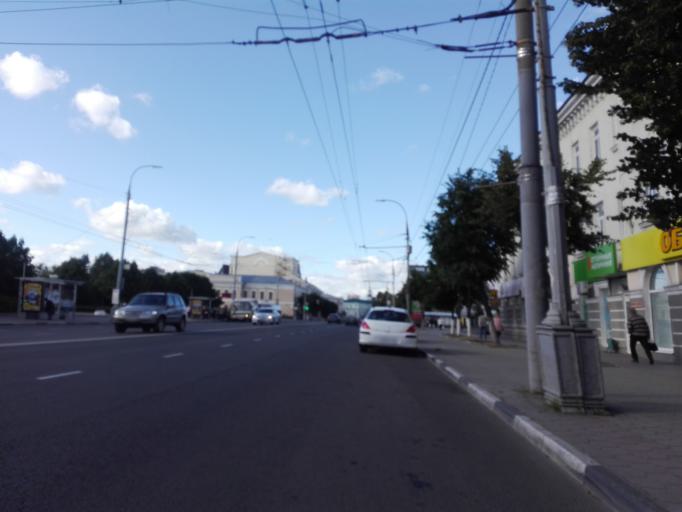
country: RU
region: Orjol
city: Orel
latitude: 52.9609
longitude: 36.0668
